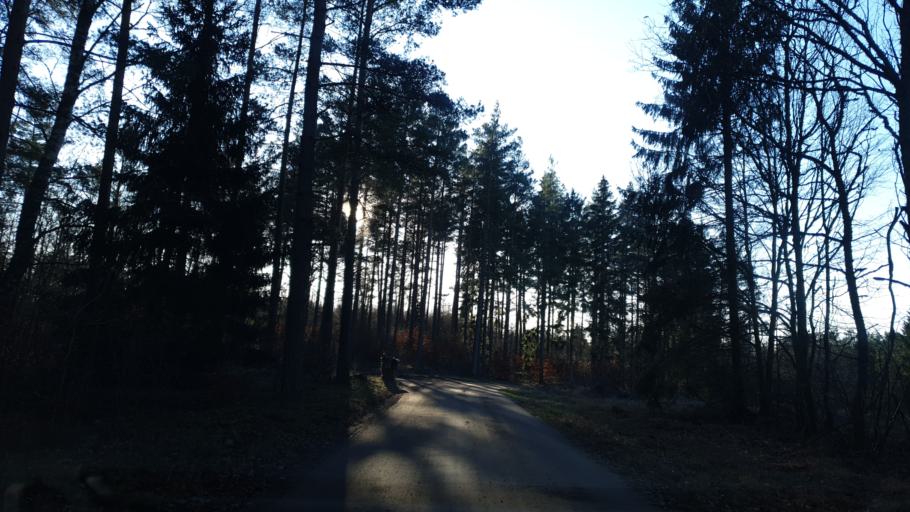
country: SE
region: Blekinge
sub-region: Karlskrona Kommun
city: Nattraby
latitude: 56.2576
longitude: 15.4111
